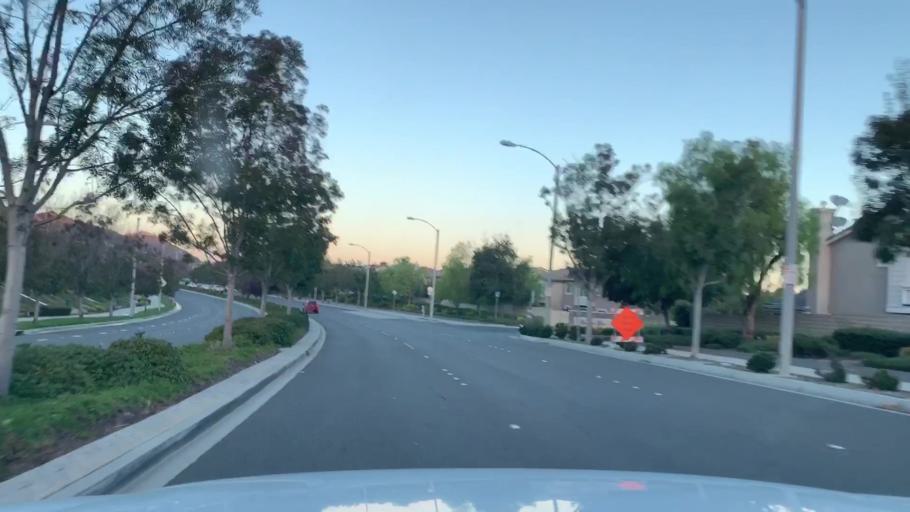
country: US
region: California
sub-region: Los Angeles County
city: Santa Clarita
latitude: 34.3953
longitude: -118.4774
